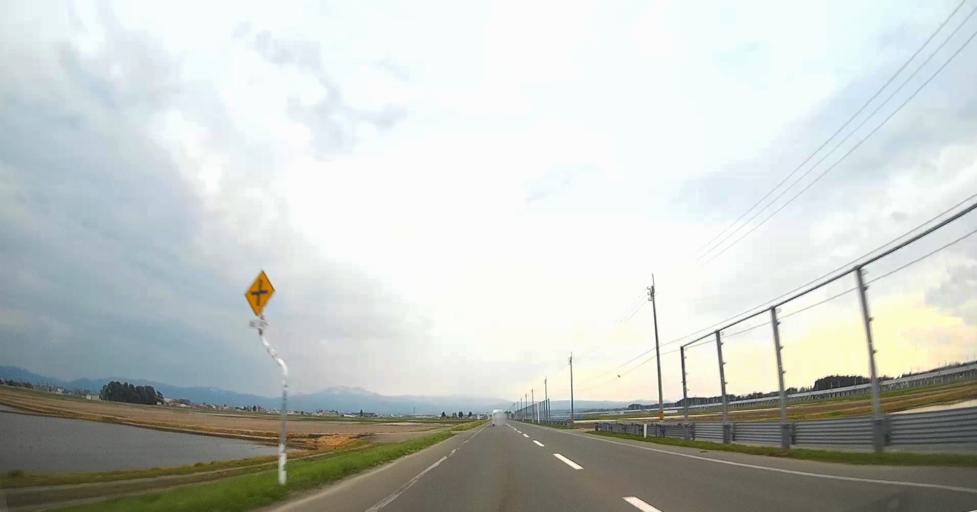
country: JP
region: Aomori
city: Aomori Shi
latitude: 40.8771
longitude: 140.6712
